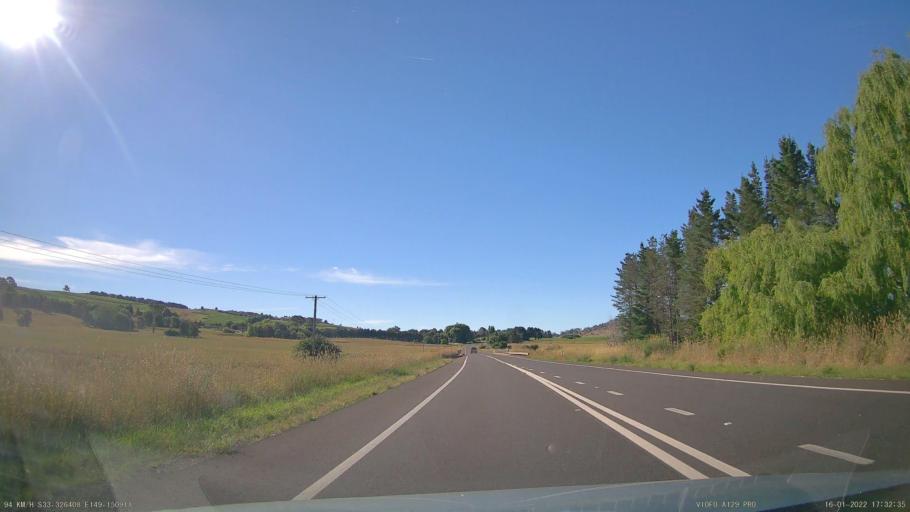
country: AU
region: New South Wales
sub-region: Orange Municipality
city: Orange
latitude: -33.3262
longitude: 149.1507
